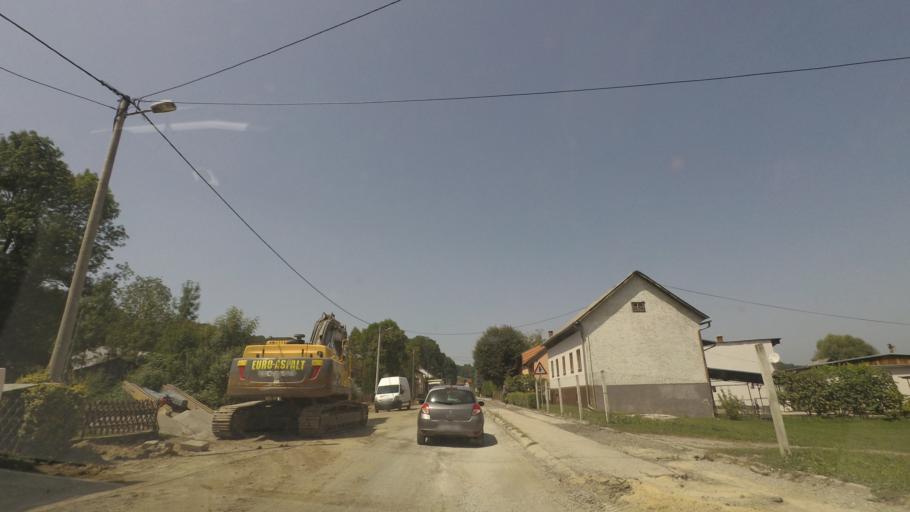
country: HR
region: Karlovacka
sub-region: Grad Karlovac
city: Karlovac
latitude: 45.4995
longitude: 15.5258
